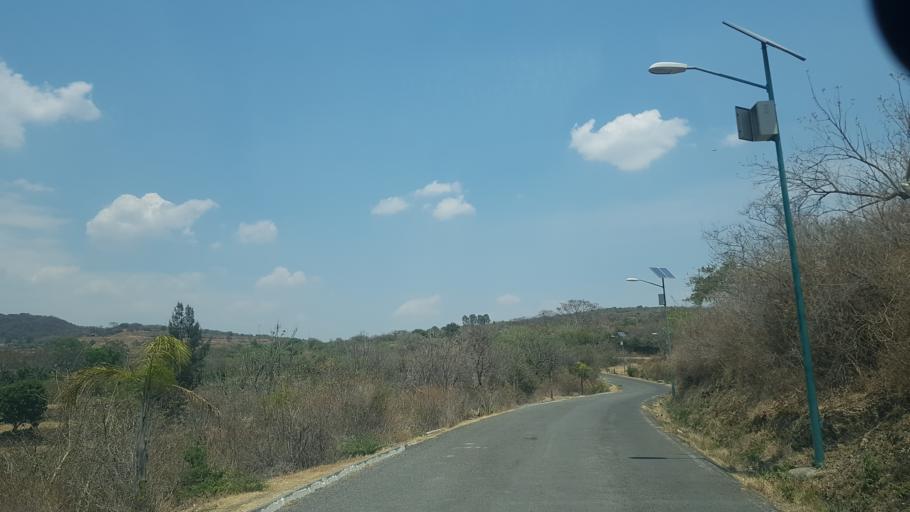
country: MX
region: Puebla
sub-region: Atzitzihuacan
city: Santiago Atzitzihuacan
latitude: 18.8350
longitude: -98.5785
